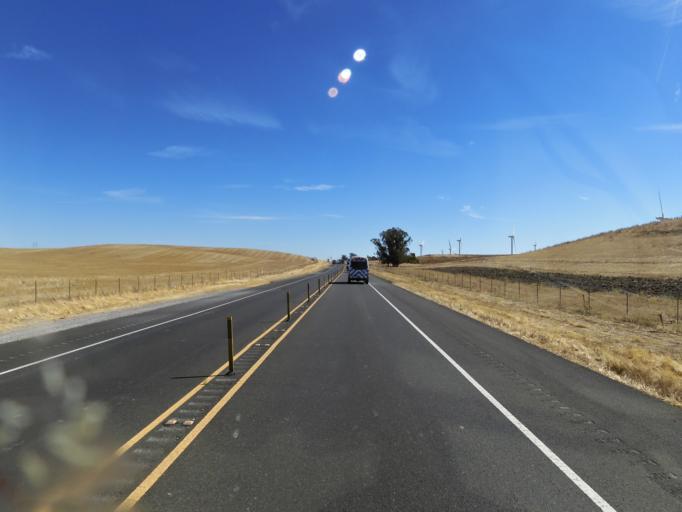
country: US
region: California
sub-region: Contra Costa County
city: Pittsburg
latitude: 38.1984
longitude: -121.8675
